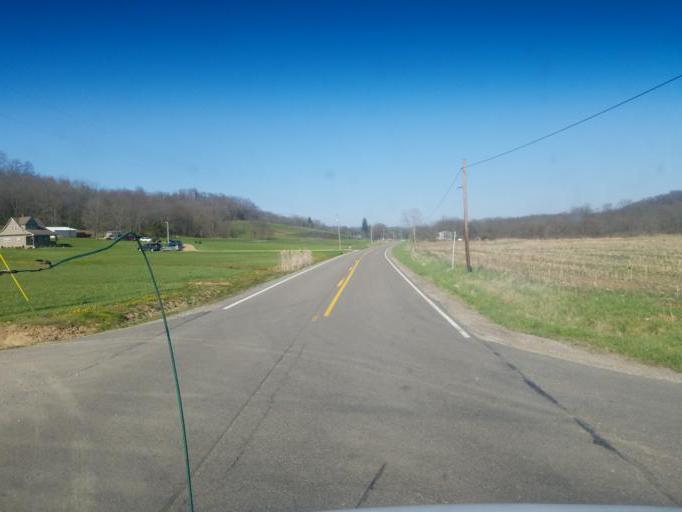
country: US
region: Ohio
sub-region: Muskingum County
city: Frazeysburg
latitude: 40.2398
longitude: -82.1476
